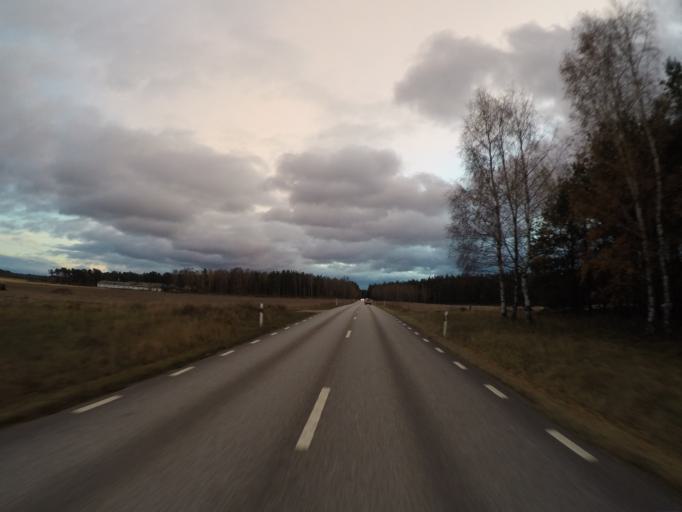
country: SE
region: Skane
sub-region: Kristianstads Kommun
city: Degeberga
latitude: 55.9211
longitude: 14.0735
